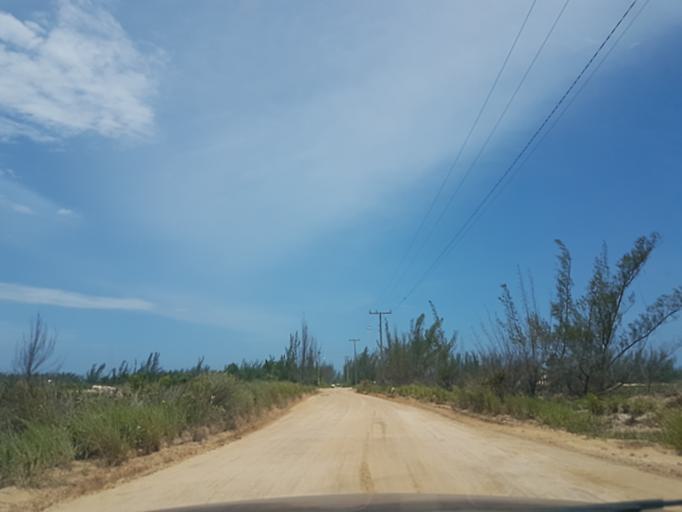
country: BR
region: Santa Catarina
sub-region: Jaguaruna
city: Jaguaruna
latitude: -28.6553
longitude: -48.9558
